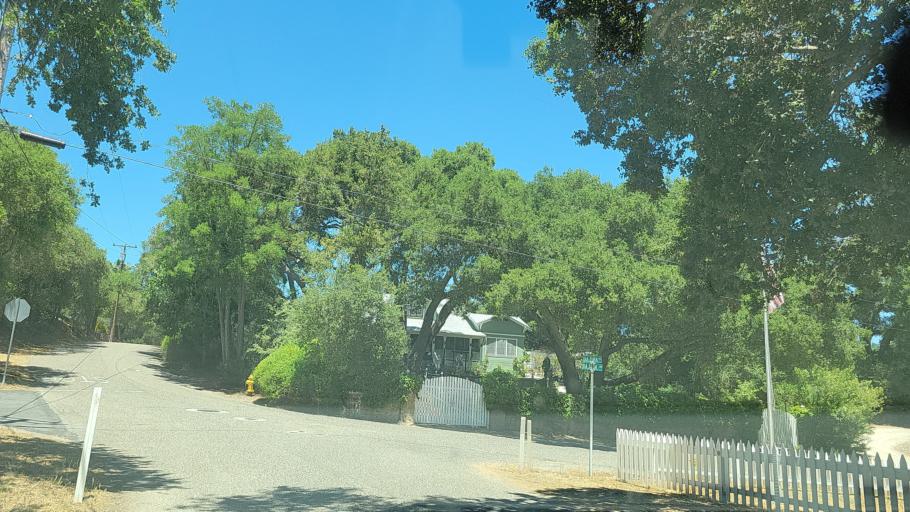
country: US
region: California
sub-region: San Luis Obispo County
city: Atascadero
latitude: 35.4986
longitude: -120.6723
